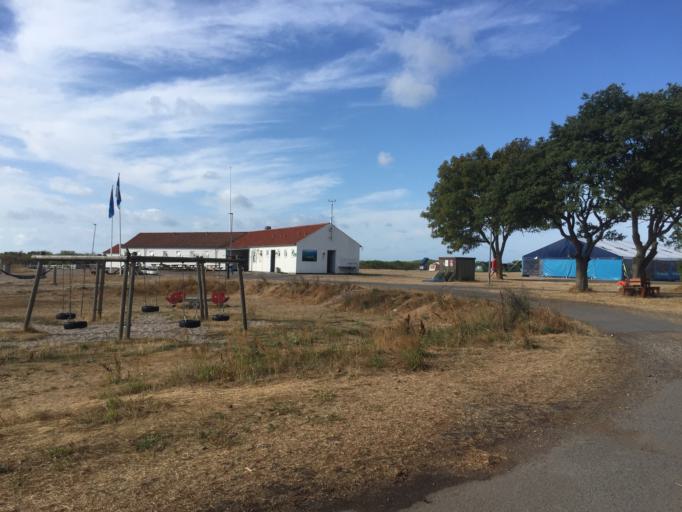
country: DK
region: Central Jutland
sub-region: Samso Kommune
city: Tranebjerg
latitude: 55.9495
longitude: 10.4518
